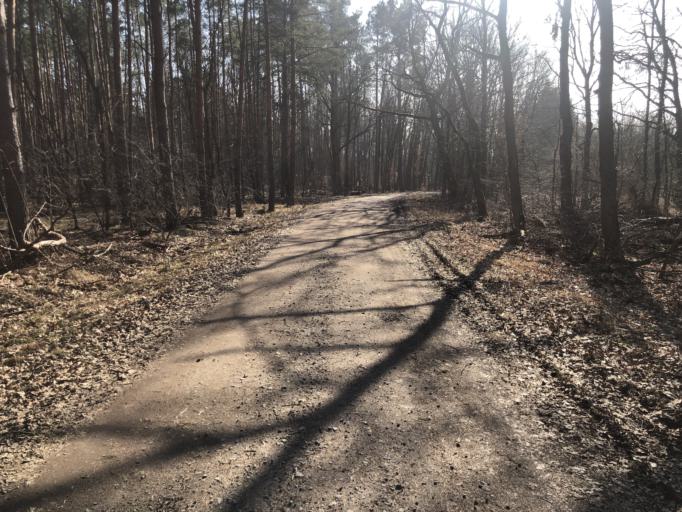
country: DE
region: Brandenburg
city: Schwerin
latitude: 52.1757
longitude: 13.5970
